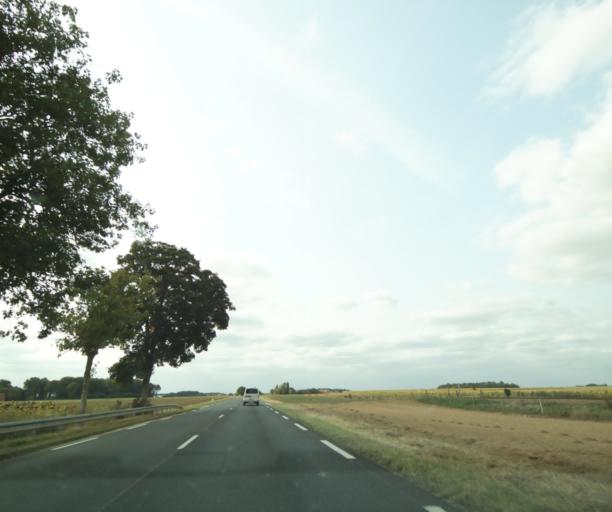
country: FR
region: Centre
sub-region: Departement d'Indre-et-Loire
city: Truyes
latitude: 47.2405
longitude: 0.8631
